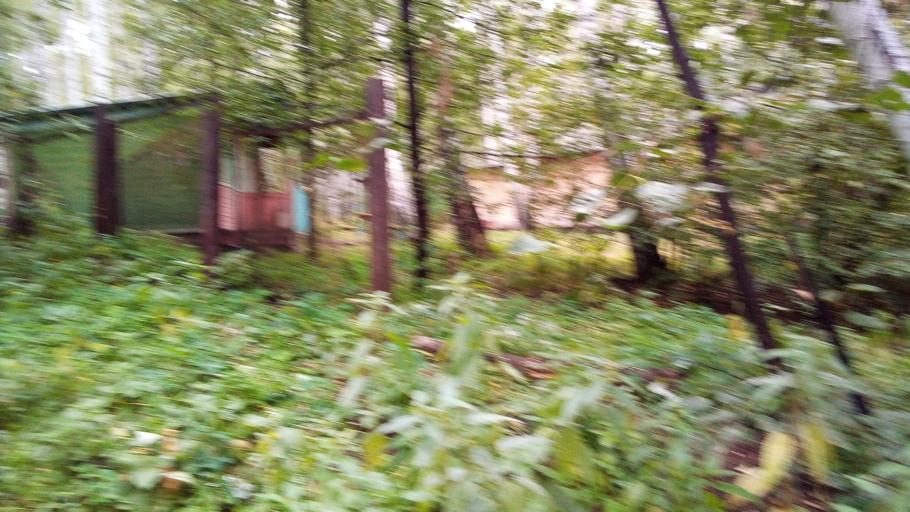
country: RU
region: Chelyabinsk
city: Tayginka
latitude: 55.4779
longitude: 60.4983
